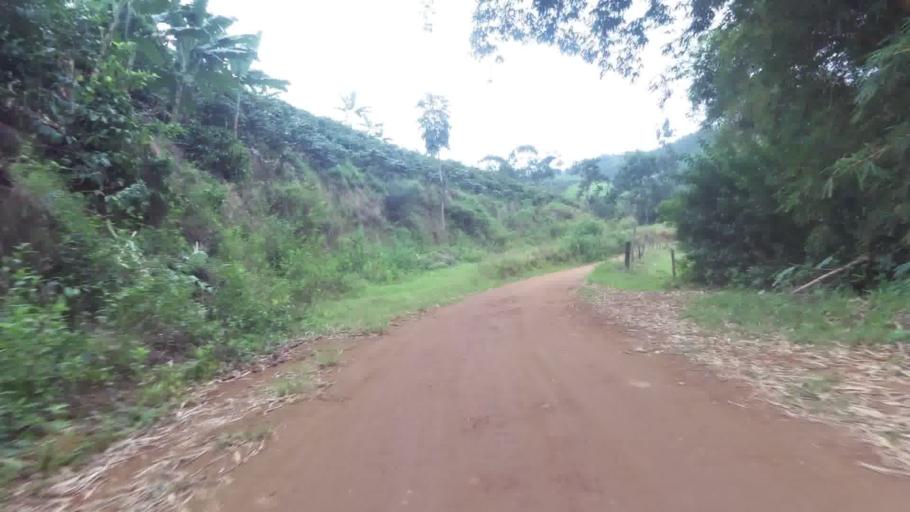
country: BR
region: Espirito Santo
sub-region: Iconha
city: Iconha
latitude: -20.7630
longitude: -40.8369
